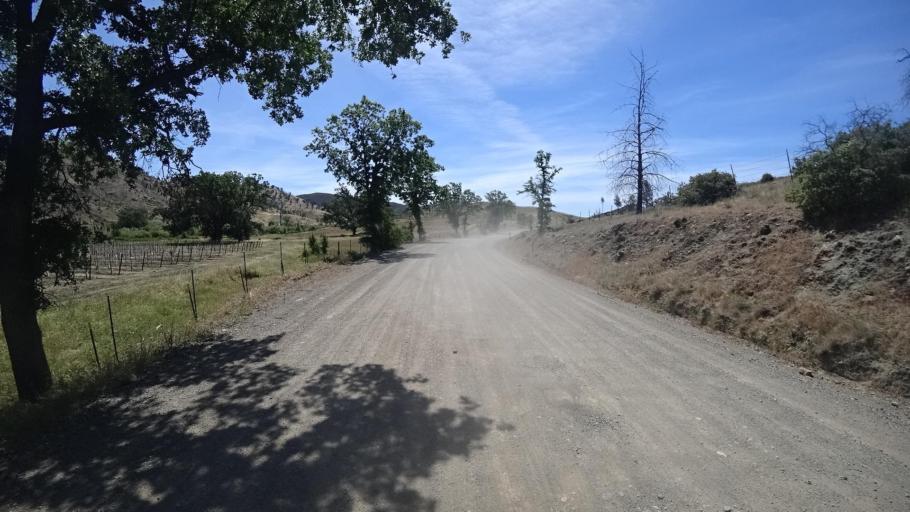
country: US
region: California
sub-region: Lake County
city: Middletown
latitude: 38.7949
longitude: -122.6146
